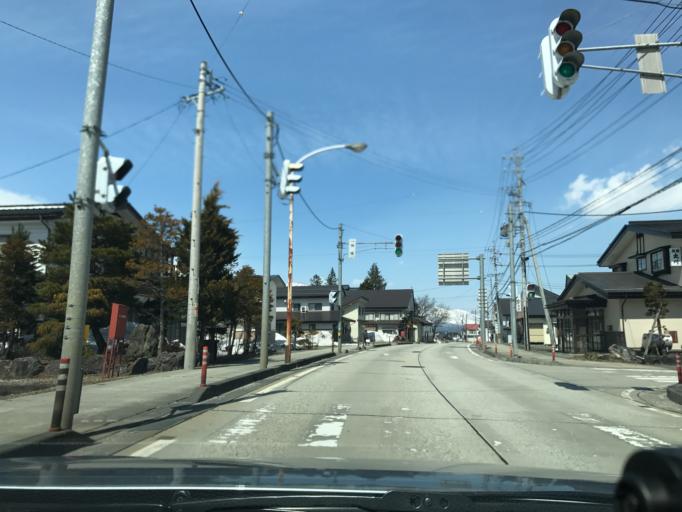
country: JP
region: Nagano
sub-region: Kitaazumi Gun
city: Hakuba
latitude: 36.6579
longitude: 137.8481
